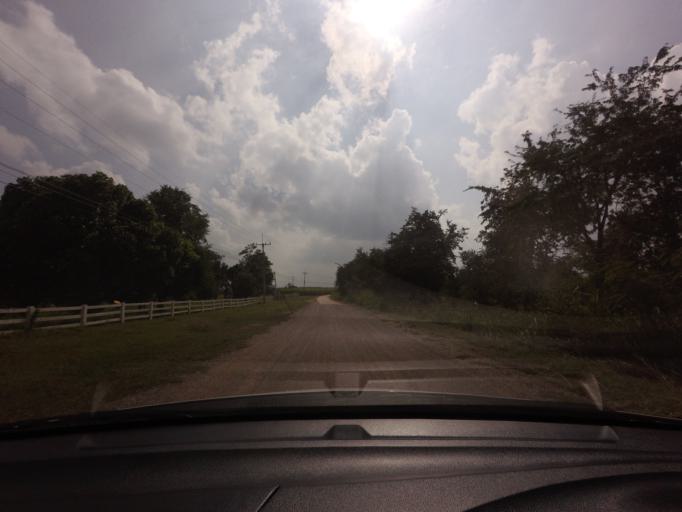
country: TH
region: Nakhon Ratchasima
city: Pak Chong
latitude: 14.5357
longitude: 101.5911
